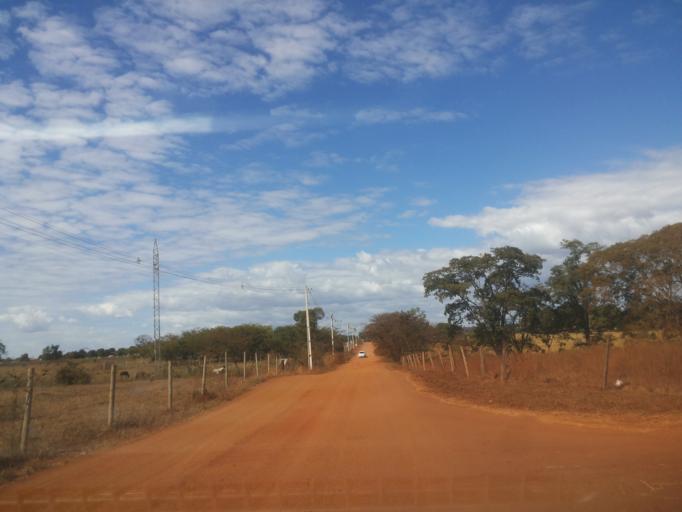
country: BR
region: Minas Gerais
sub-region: Centralina
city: Centralina
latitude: -18.5770
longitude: -49.2138
